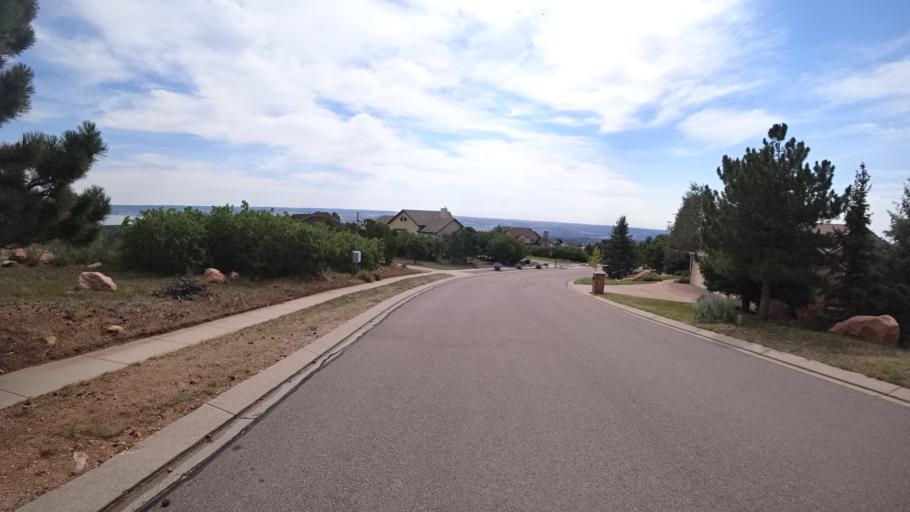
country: US
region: Colorado
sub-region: El Paso County
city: Air Force Academy
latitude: 38.9538
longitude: -104.8866
